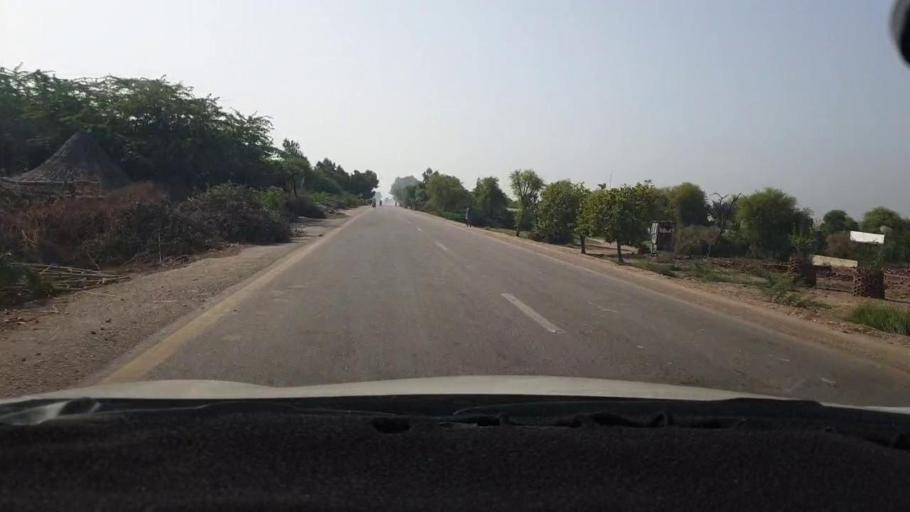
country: PK
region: Sindh
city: Sanghar
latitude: 25.9978
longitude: 68.9632
